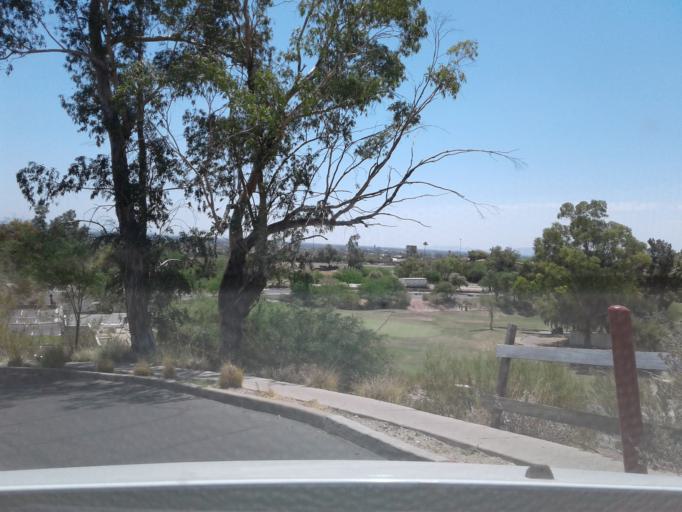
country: US
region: Arizona
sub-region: Maricopa County
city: Guadalupe
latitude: 33.3698
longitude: -111.9725
